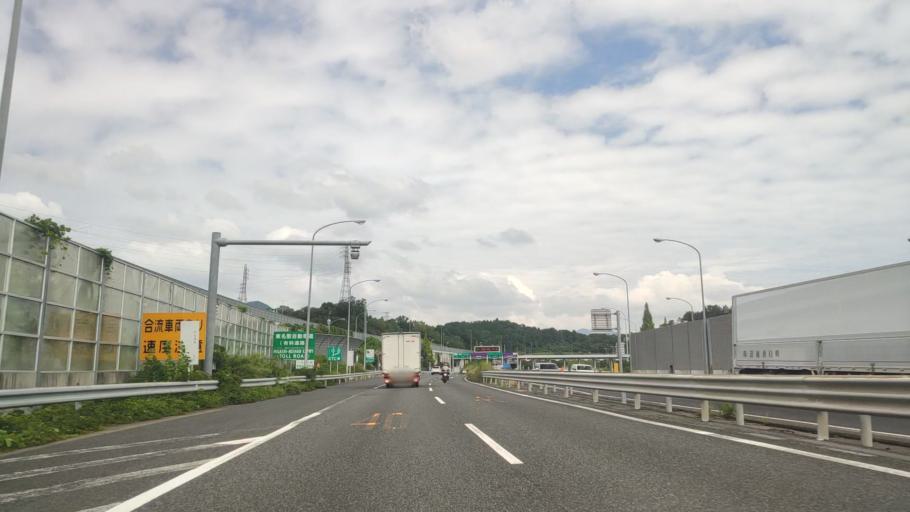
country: JP
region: Mie
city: Kameyama
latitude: 34.8588
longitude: 136.4139
